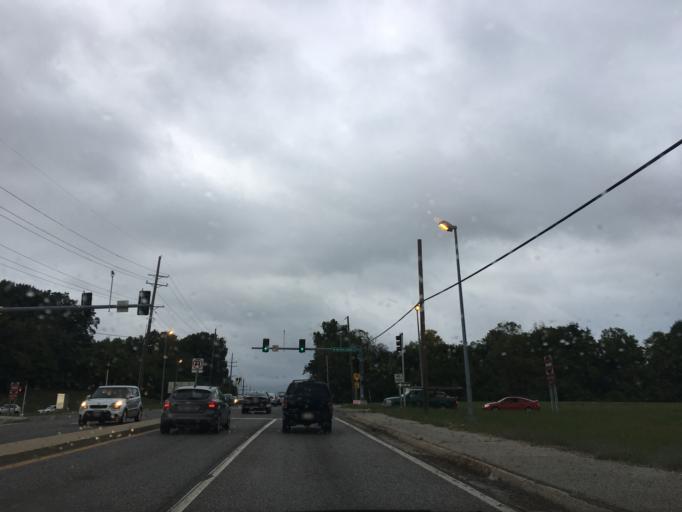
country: US
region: Missouri
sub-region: Saint Louis County
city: Saint Ann
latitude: 38.7232
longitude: -90.4070
